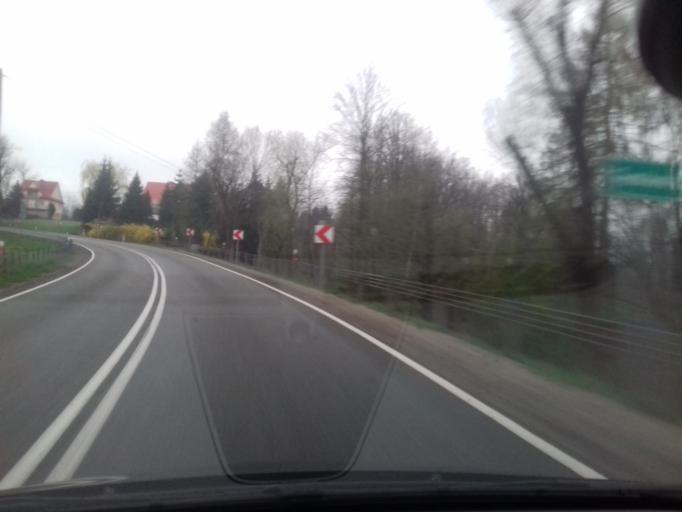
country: PL
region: Lesser Poland Voivodeship
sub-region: Powiat limanowski
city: Tymbark
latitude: 49.7233
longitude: 20.3318
